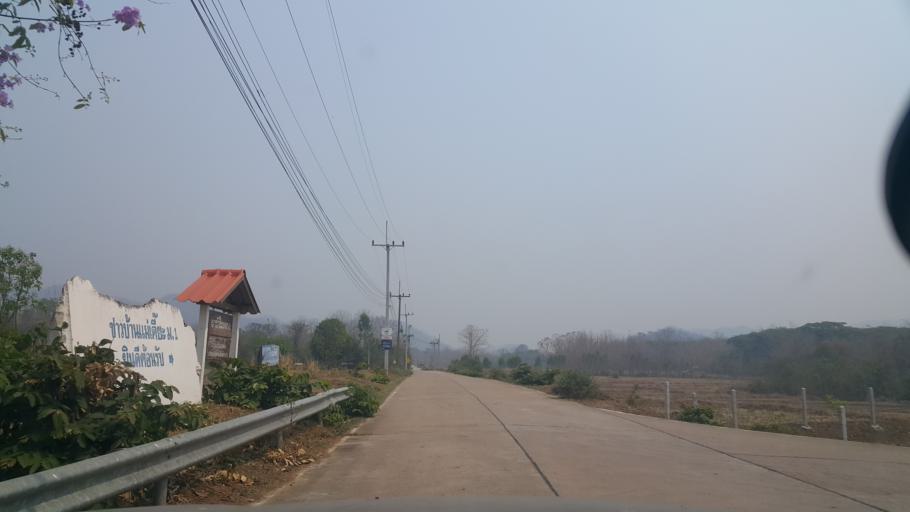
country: TH
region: Lampang
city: Sop Prap
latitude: 17.7977
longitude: 99.2620
